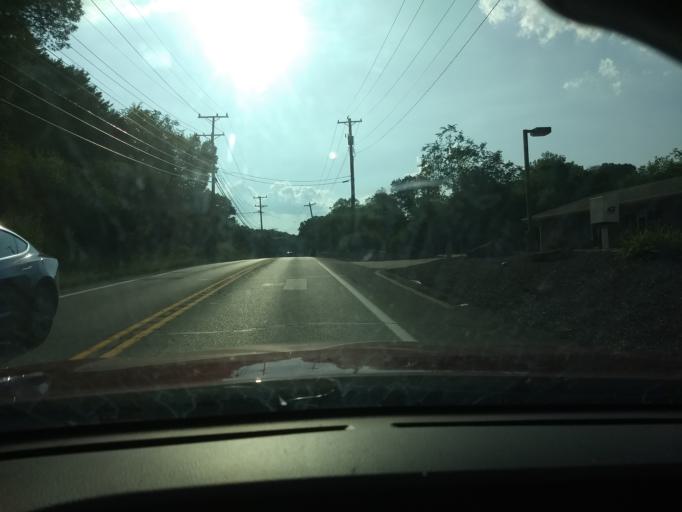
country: US
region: Pennsylvania
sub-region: Allegheny County
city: Bakerstown
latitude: 40.6186
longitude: -79.9070
